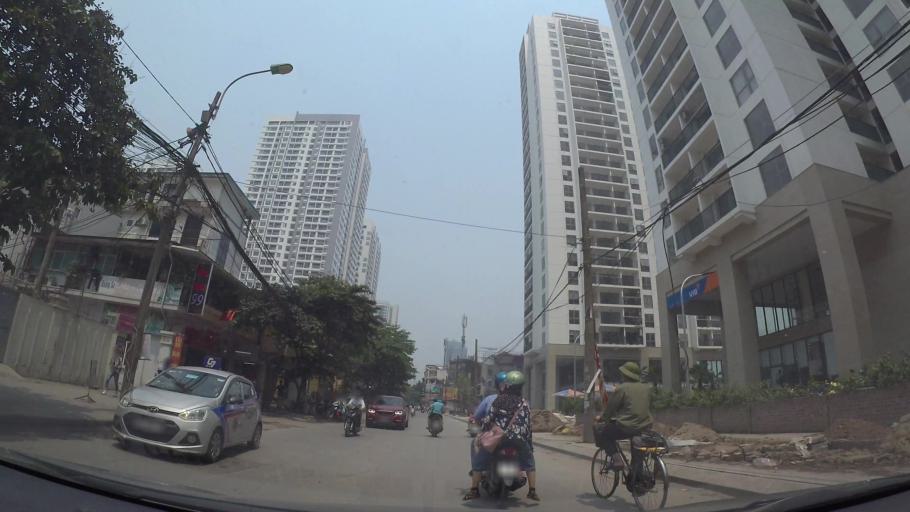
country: VN
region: Ha Noi
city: Thanh Xuan
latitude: 20.9965
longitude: 105.8048
